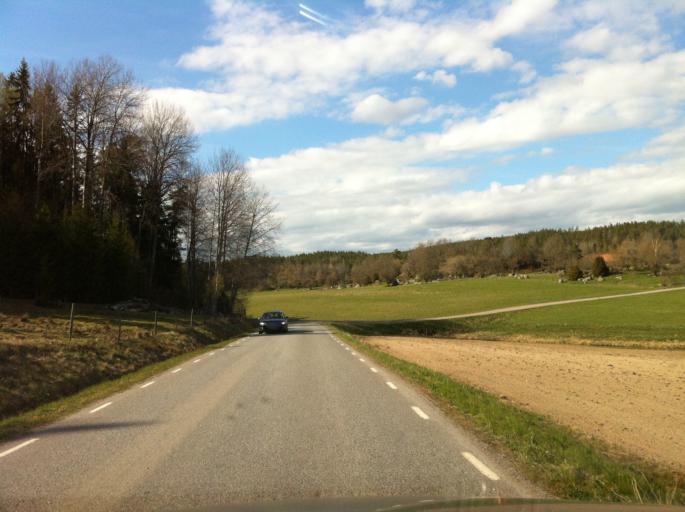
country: SE
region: Kalmar
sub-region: Vimmerby Kommun
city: Sodra Vi
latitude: 57.8789
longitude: 15.8395
